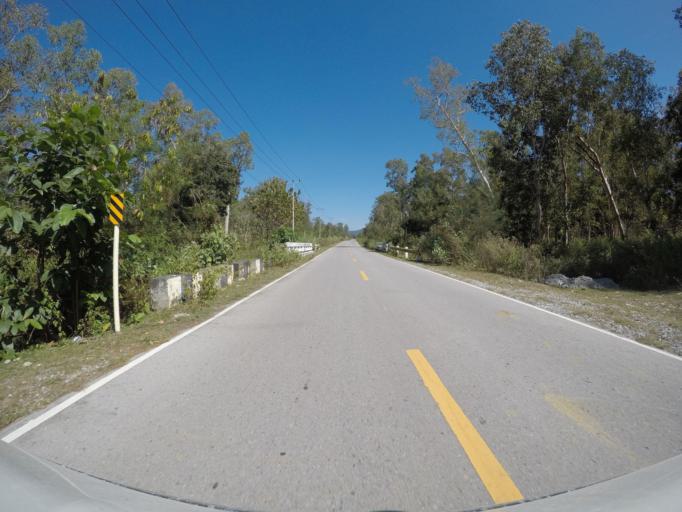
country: TL
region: Viqueque
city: Viqueque
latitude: -8.9694
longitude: 126.0285
